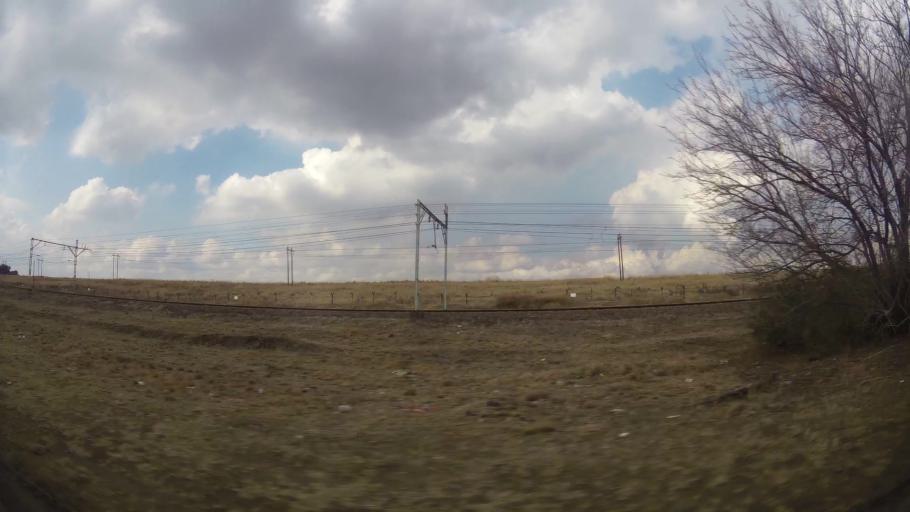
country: ZA
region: Gauteng
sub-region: Sedibeng District Municipality
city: Vereeniging
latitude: -26.7022
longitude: 27.9337
